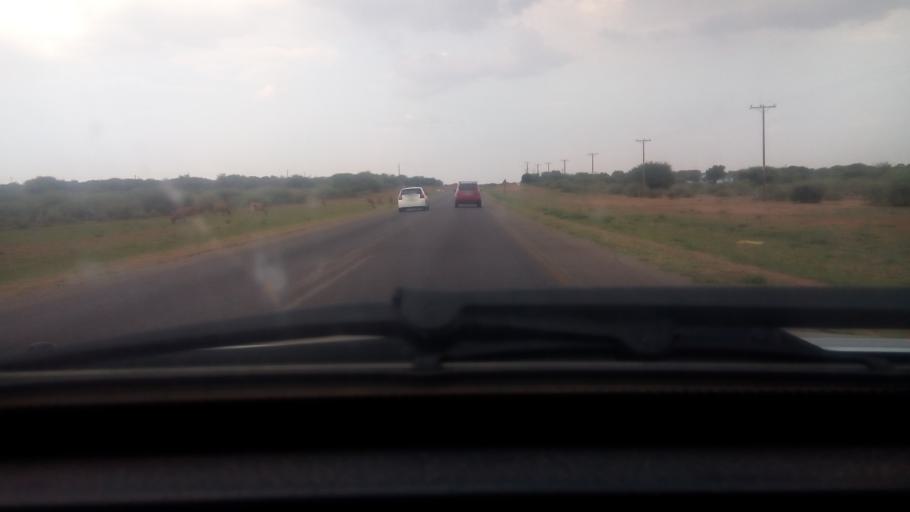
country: BW
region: Kweneng
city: Metsemotlhaba
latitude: -24.4649
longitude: 25.6660
